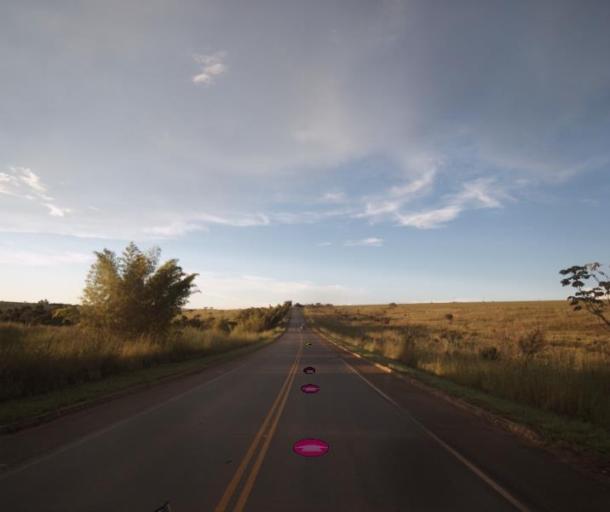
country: BR
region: Goias
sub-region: Anapolis
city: Anapolis
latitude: -16.1798
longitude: -48.9019
